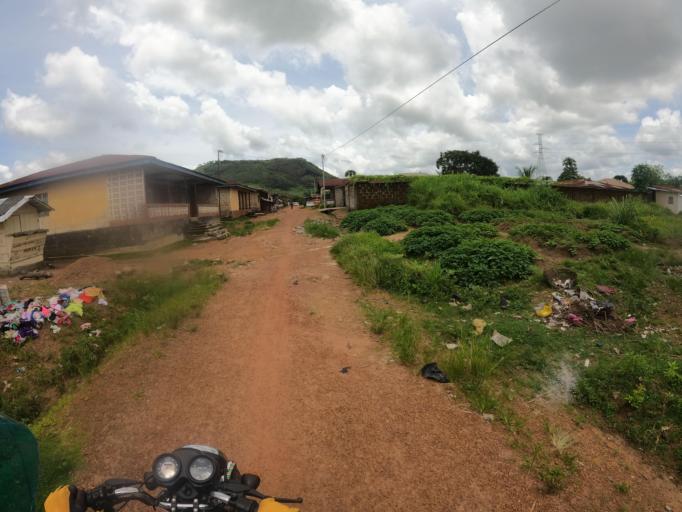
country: SL
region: Northern Province
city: Makeni
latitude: 8.8922
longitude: -12.0504
